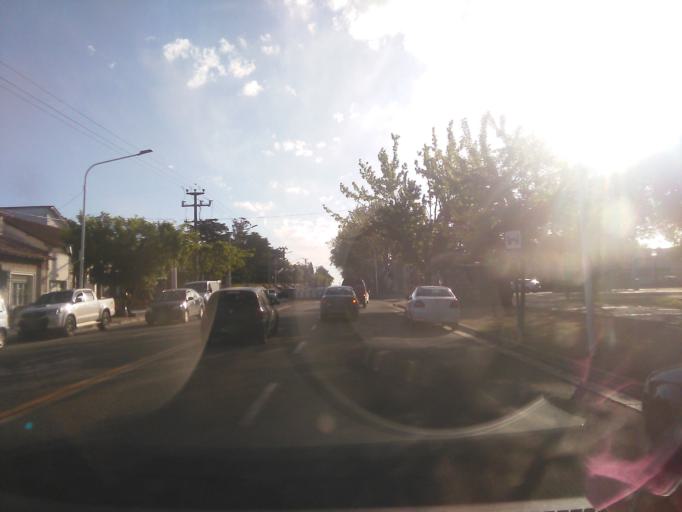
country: AR
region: Buenos Aires
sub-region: Partido de Tandil
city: Tandil
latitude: -37.3347
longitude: -59.1357
